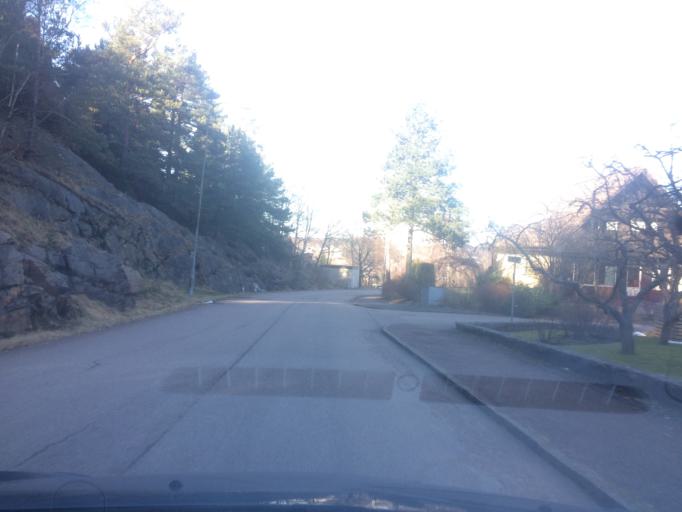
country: SE
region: Vaestra Goetaland
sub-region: Goteborg
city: Goeteborg
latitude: 57.7459
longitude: 11.9327
